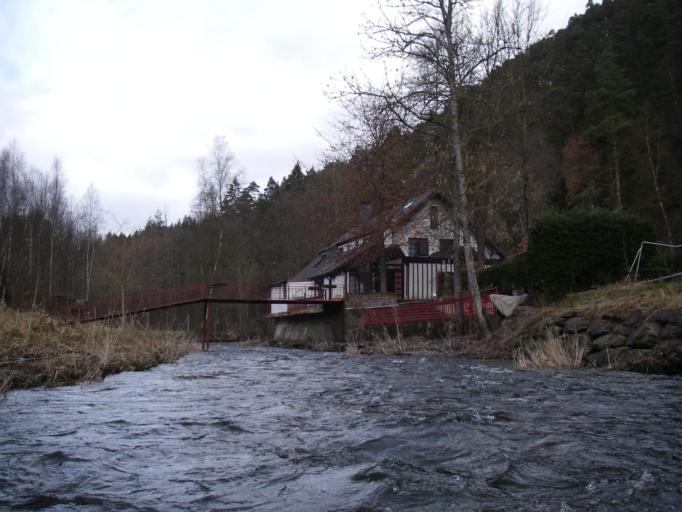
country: BE
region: Wallonia
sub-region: Province du Luxembourg
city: Vielsalm
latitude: 50.3069
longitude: 5.9107
